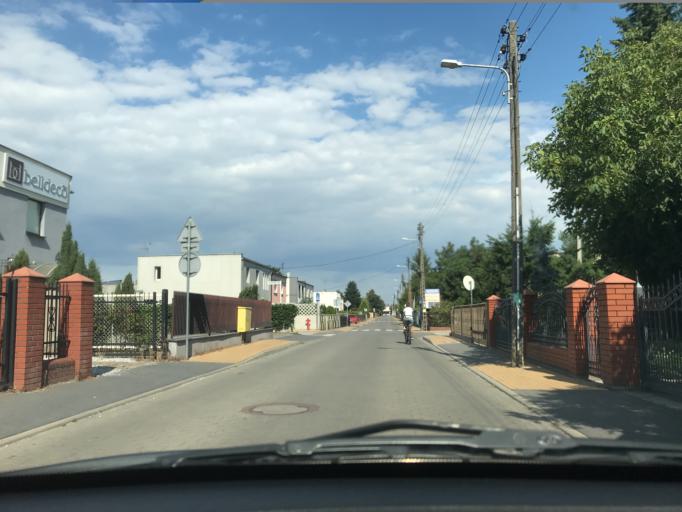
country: PL
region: Greater Poland Voivodeship
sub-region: Powiat poznanski
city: Plewiska
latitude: 52.3702
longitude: 16.8244
